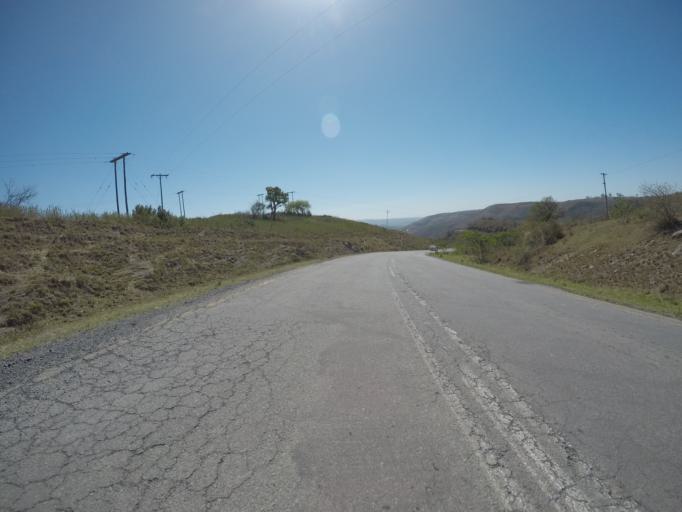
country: ZA
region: Eastern Cape
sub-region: OR Tambo District Municipality
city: Mthatha
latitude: -31.9106
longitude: 28.9578
